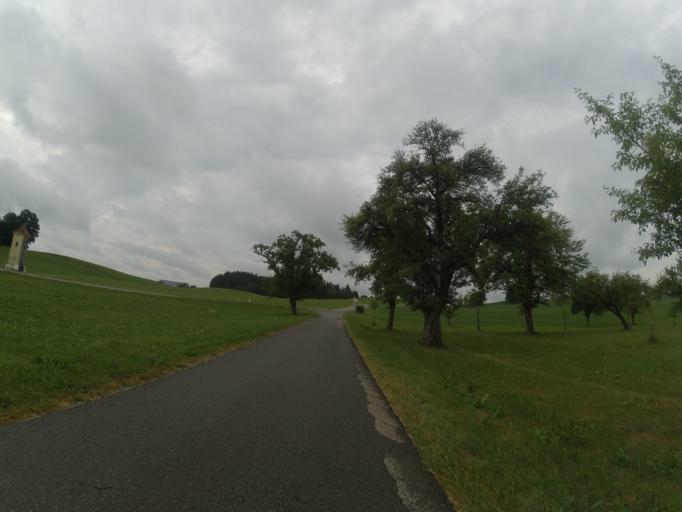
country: DE
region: Baden-Wuerttemberg
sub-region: Tuebingen Region
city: Kisslegg
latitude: 47.7456
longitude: 9.8517
